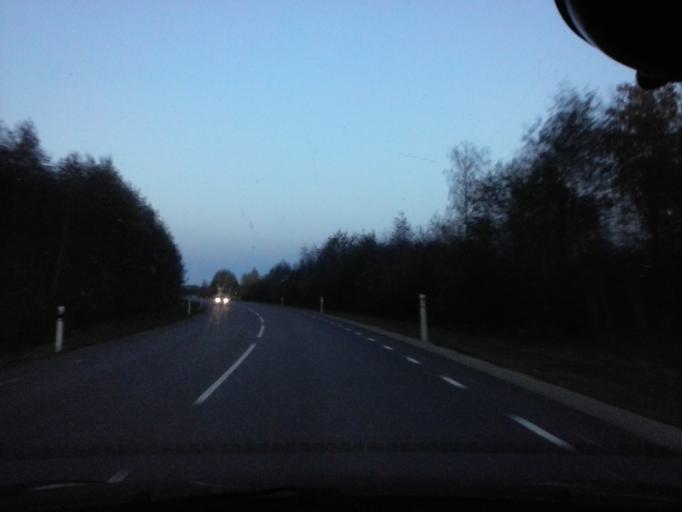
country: EE
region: Raplamaa
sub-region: Rapla vald
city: Rapla
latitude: 58.9897
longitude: 24.7588
